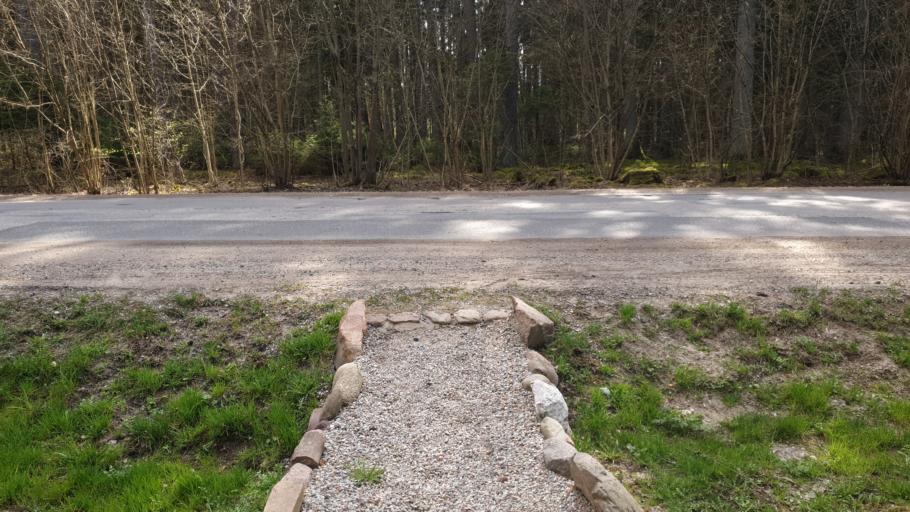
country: LT
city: Aukstadvaris
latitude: 54.4977
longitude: 24.6522
